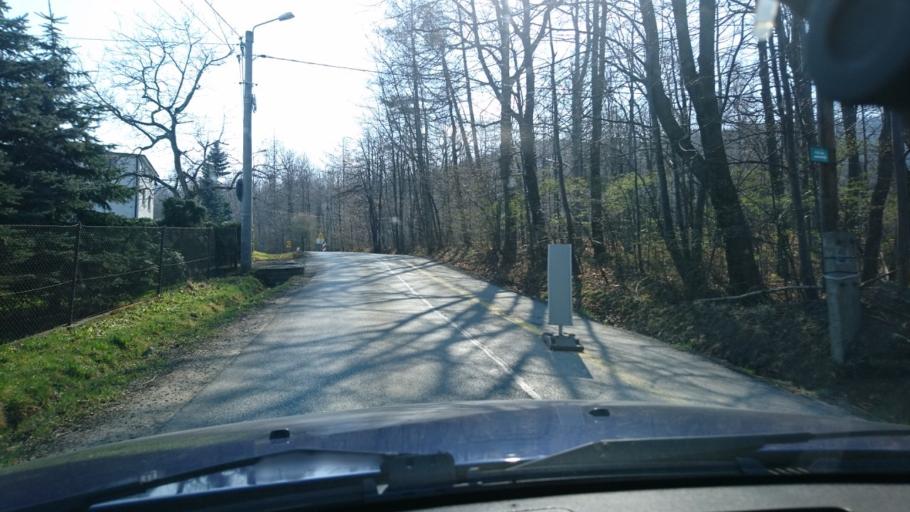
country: PL
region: Silesian Voivodeship
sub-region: Powiat bielski
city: Kozy
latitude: 49.8192
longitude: 19.1123
